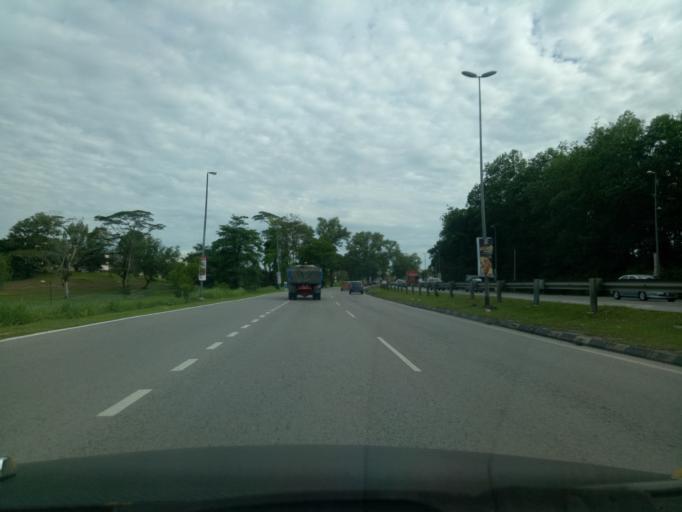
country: MY
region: Sarawak
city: Kuching
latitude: 1.4500
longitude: 110.3267
